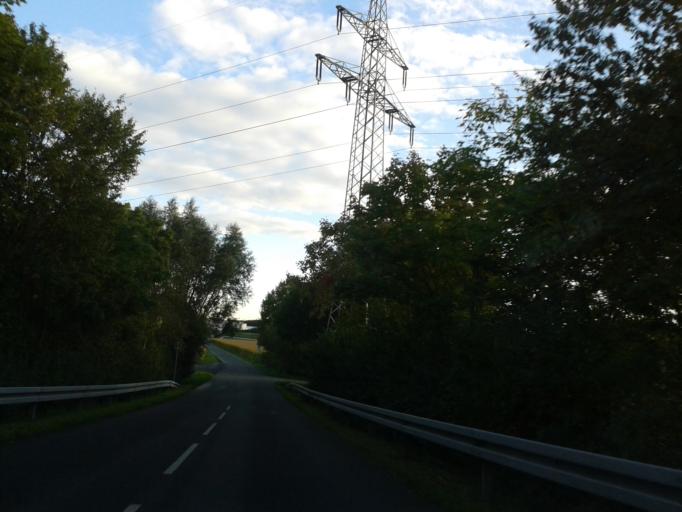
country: DE
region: North Rhine-Westphalia
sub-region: Regierungsbezirk Detmold
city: Paderborn
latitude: 51.7372
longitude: 8.7139
